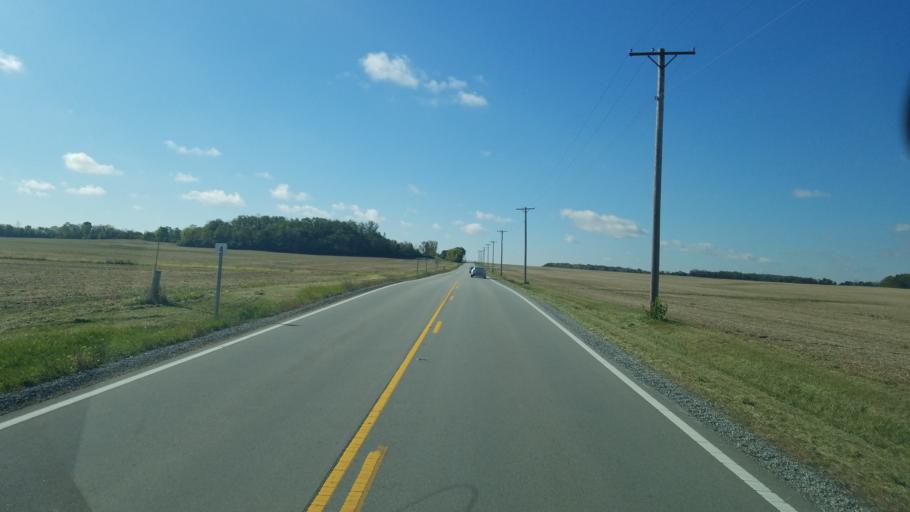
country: US
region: Ohio
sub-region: Highland County
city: Leesburg
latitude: 39.4308
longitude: -83.5139
